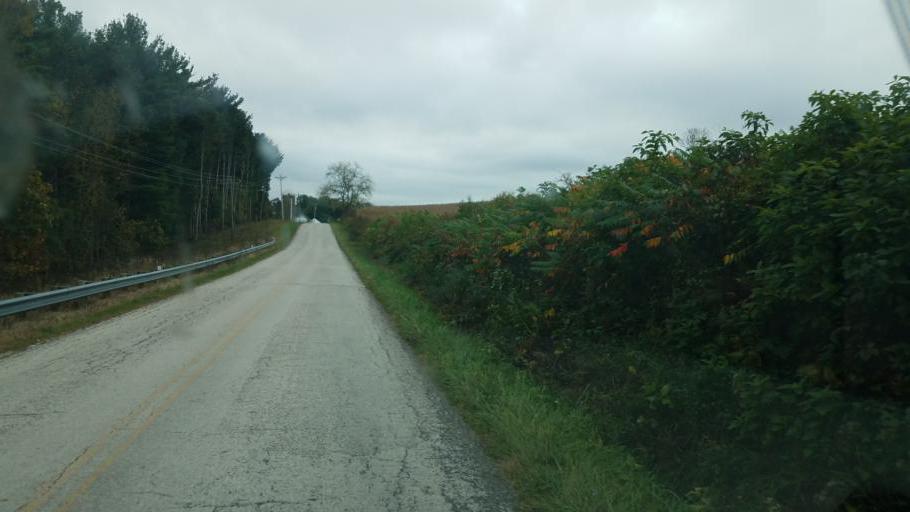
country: US
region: Ohio
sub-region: Ashland County
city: Loudonville
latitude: 40.5723
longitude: -82.1656
